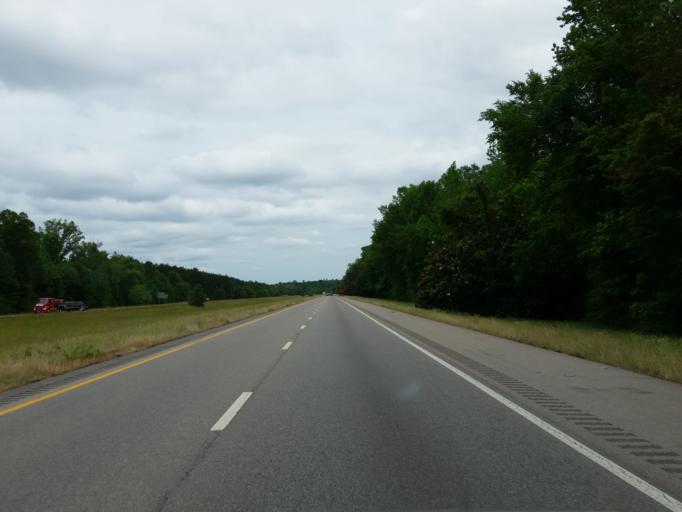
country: US
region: Mississippi
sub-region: Lauderdale County
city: Marion
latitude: 32.4123
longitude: -88.4891
